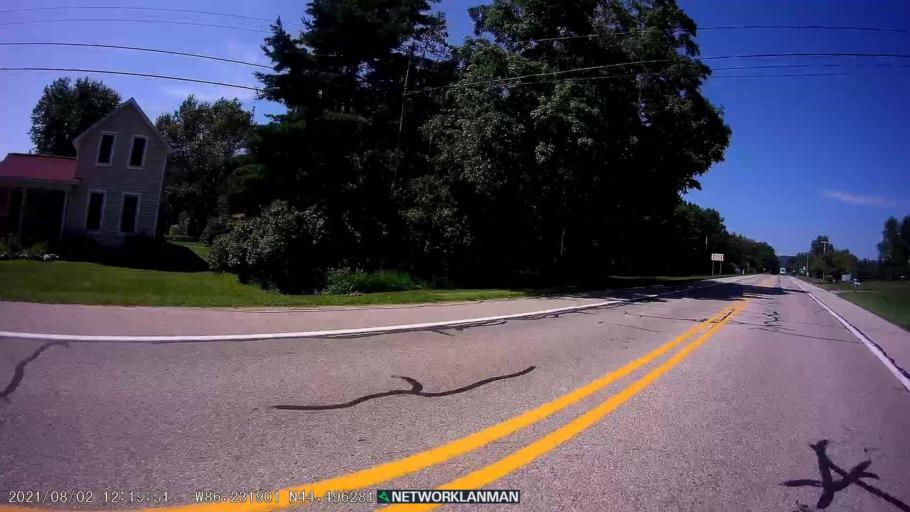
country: US
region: Michigan
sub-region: Benzie County
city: Frankfort
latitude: 44.4965
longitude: -86.2319
